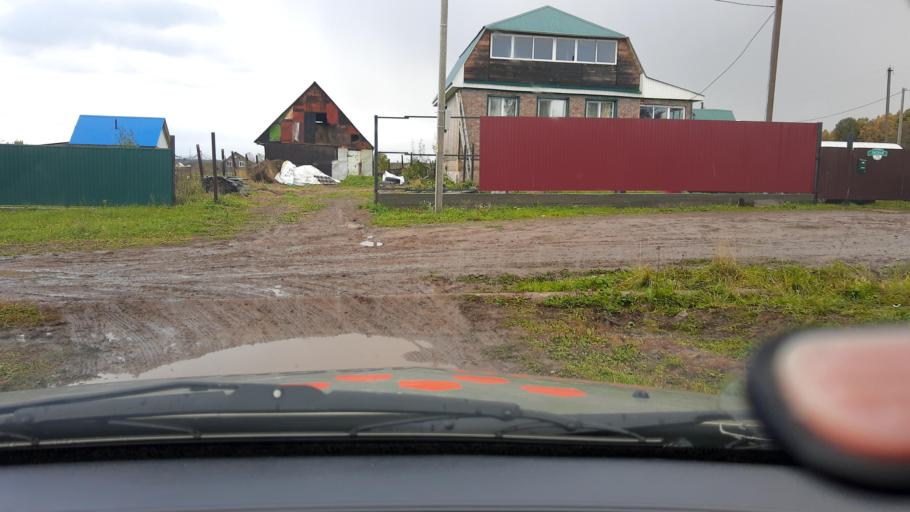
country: RU
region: Bashkortostan
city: Kudeyevskiy
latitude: 54.8747
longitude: 56.6272
